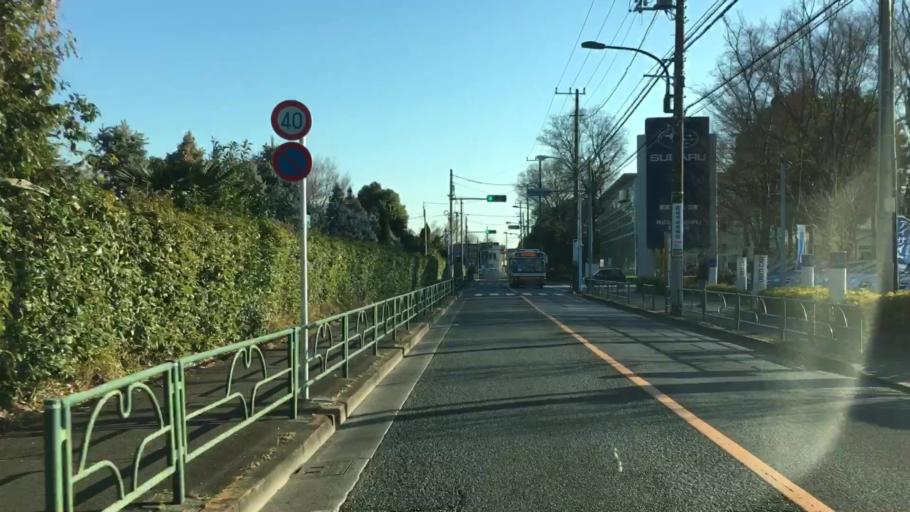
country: JP
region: Tokyo
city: Mitaka-shi
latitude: 35.6860
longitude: 139.5386
